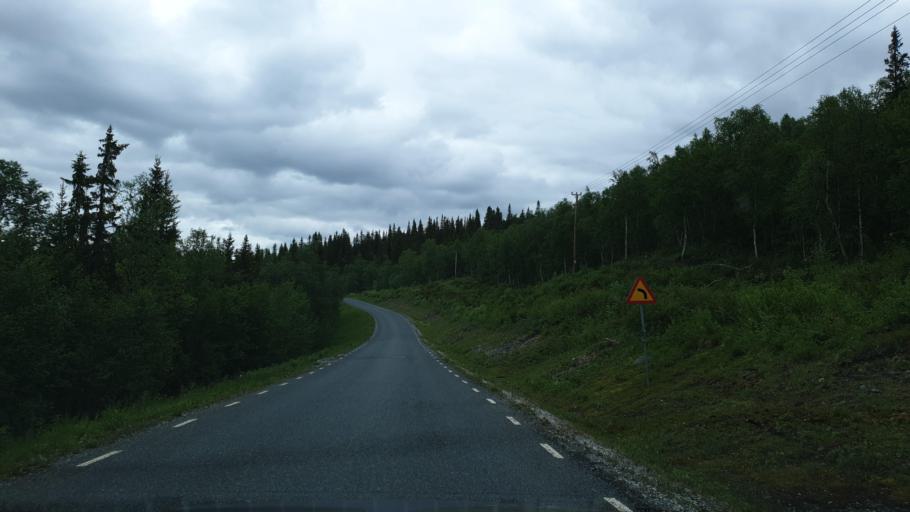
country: SE
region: Vaesterbotten
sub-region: Vilhelmina Kommun
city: Sjoberg
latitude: 65.2924
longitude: 15.2931
